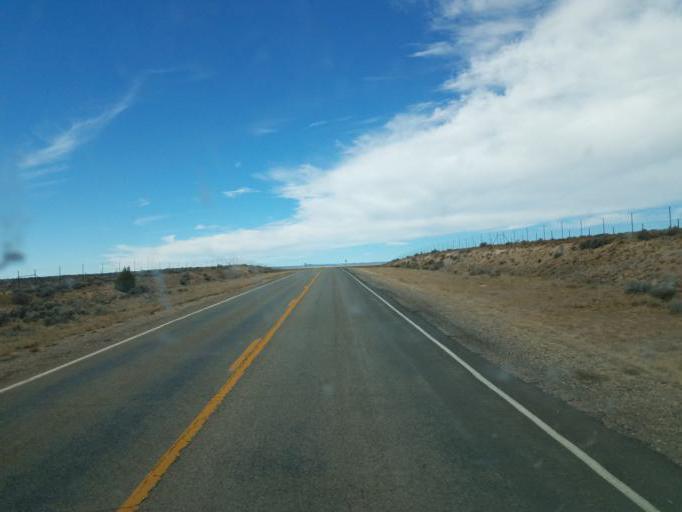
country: US
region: New Mexico
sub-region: Taos County
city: Arroyo Seco
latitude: 36.4738
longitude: -105.7130
